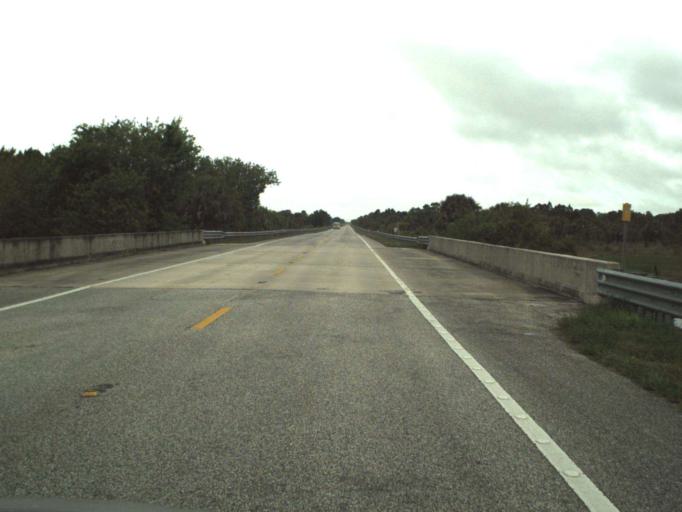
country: US
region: Florida
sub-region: Seminole County
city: Geneva
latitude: 28.6976
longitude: -81.0057
